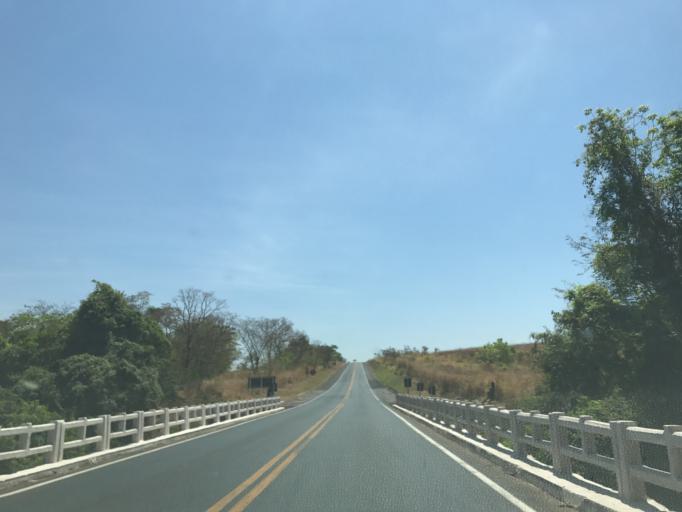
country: BR
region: Minas Gerais
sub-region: Prata
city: Prata
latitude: -19.5184
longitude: -48.8358
